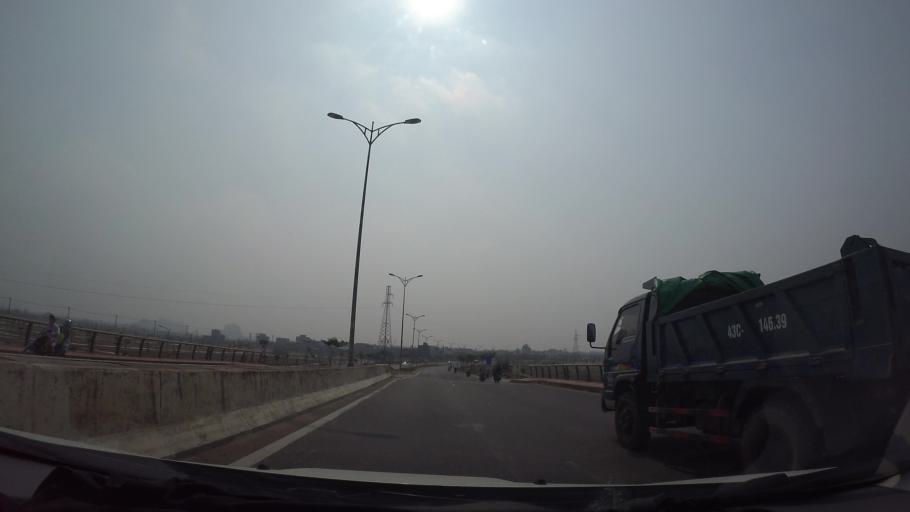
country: VN
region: Da Nang
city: Ngu Hanh Son
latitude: 16.0005
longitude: 108.2307
